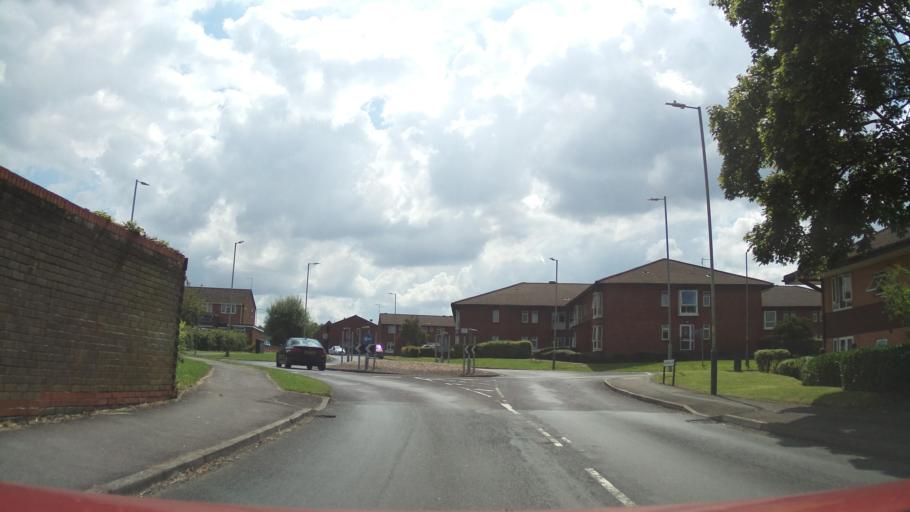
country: GB
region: England
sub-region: Wiltshire
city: Lydiard Tregoze
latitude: 51.5552
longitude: -1.8371
